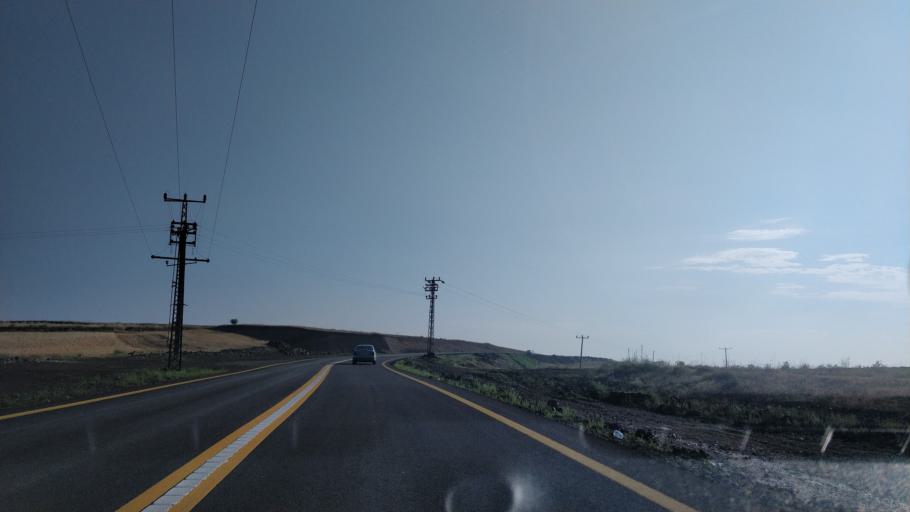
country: TR
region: Ankara
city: Etimesgut
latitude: 39.8605
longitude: 32.5724
